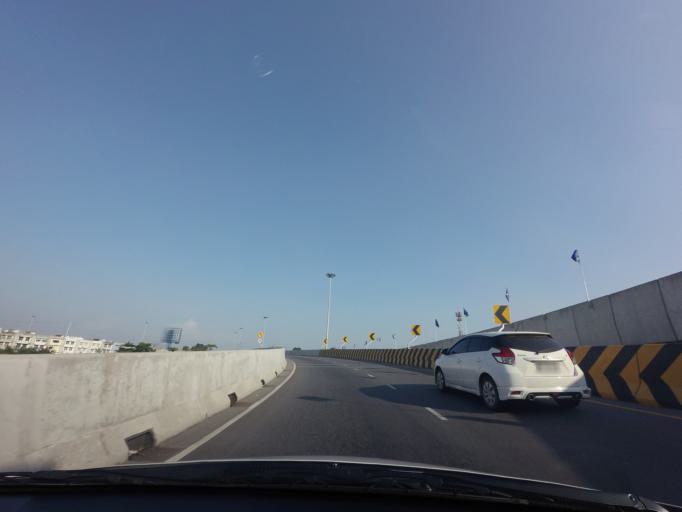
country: TH
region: Bangkok
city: Taling Chan
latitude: 13.7984
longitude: 100.4077
